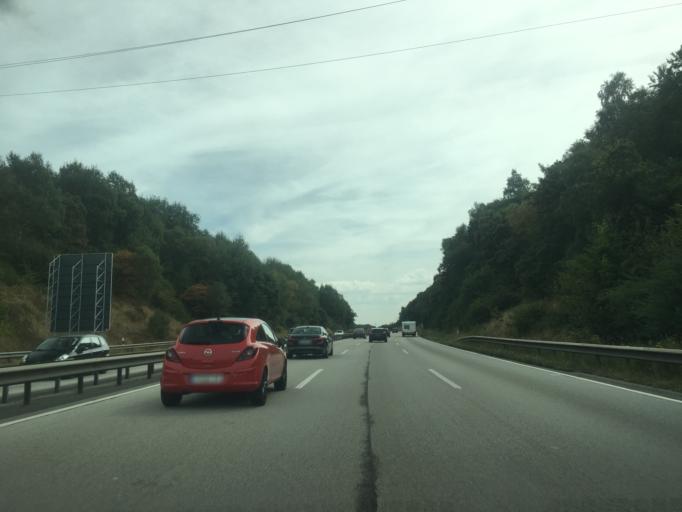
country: DE
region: Rheinland-Pfalz
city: Dichtelbach
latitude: 49.9920
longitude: 7.6960
